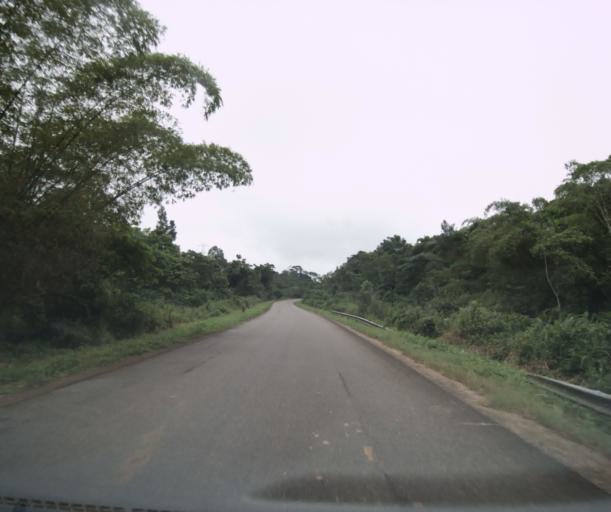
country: CM
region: Littoral
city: Edea
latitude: 3.6670
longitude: 10.1117
